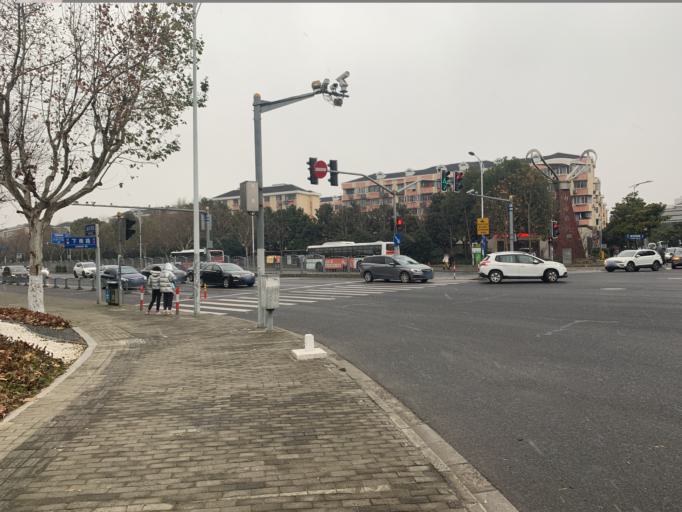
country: CN
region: Shanghai Shi
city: Huamu
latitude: 31.1895
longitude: 121.5294
